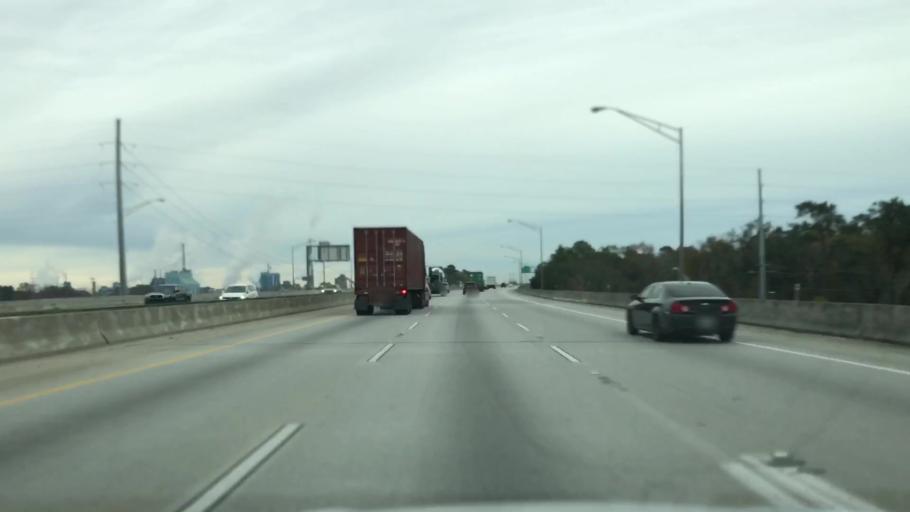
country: US
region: South Carolina
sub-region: Charleston County
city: North Charleston
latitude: 32.8941
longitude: -79.9865
